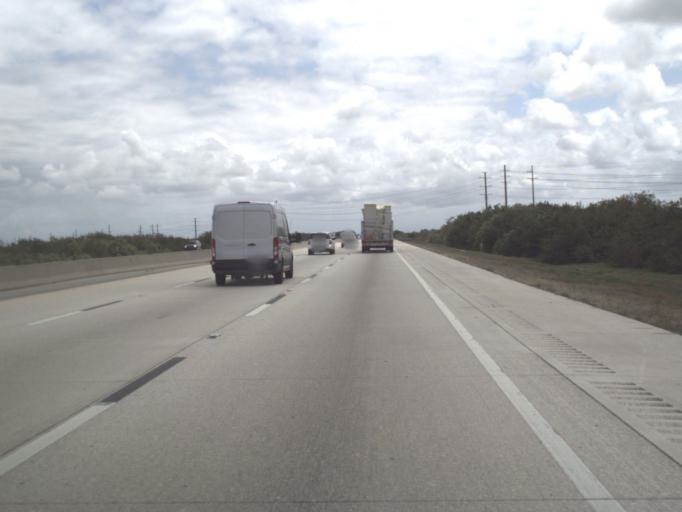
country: US
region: Florida
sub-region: Brevard County
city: Cocoa West
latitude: 28.3322
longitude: -80.7766
